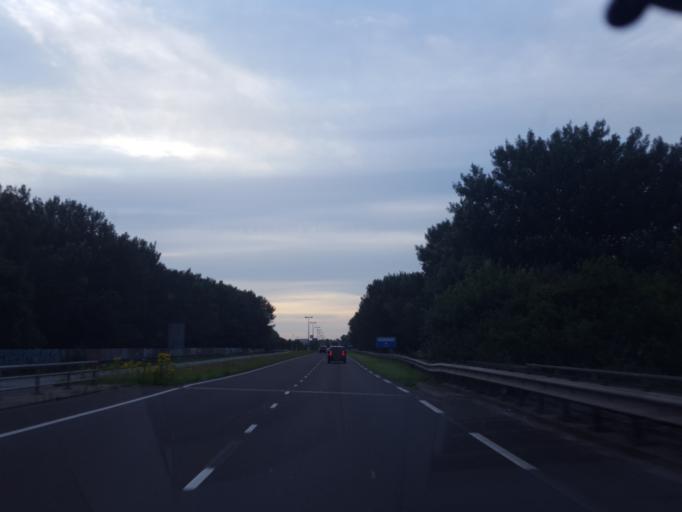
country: NL
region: Friesland
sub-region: Gemeente Leeuwarden
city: Camminghaburen
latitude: 53.2026
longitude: 5.8362
